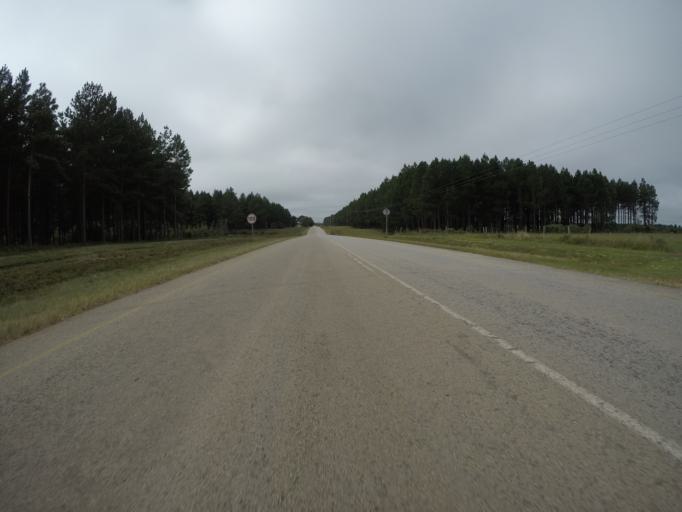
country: ZA
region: Eastern Cape
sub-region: Cacadu District Municipality
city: Kareedouw
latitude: -33.9954
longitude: 24.1284
